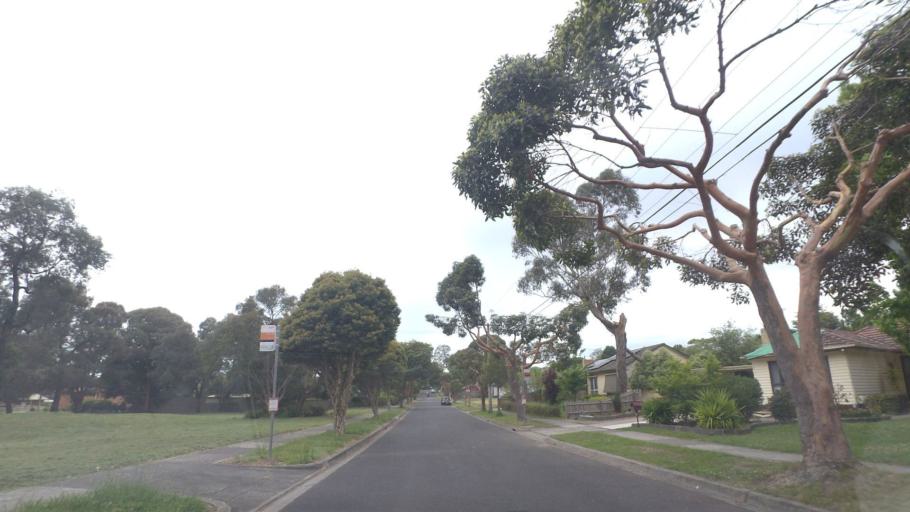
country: AU
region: Victoria
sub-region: Yarra Ranges
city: Kilsyth
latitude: -37.7947
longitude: 145.3068
